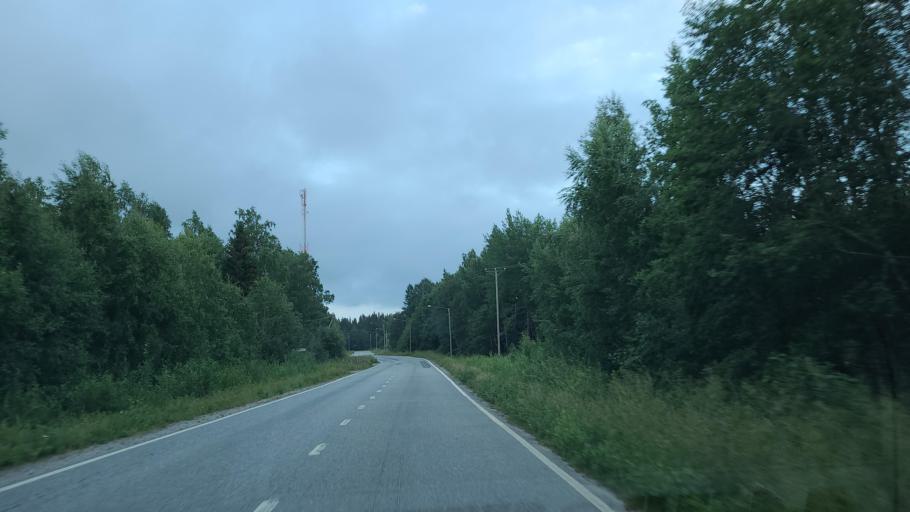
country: FI
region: Ostrobothnia
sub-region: Vaasa
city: Replot
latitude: 63.2888
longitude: 21.1145
